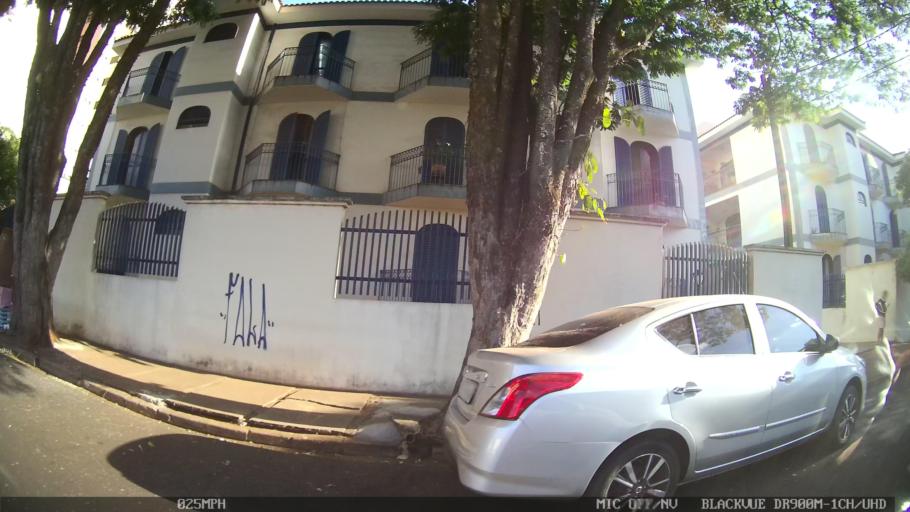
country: BR
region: Sao Paulo
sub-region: Ribeirao Preto
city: Ribeirao Preto
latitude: -21.1842
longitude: -47.7890
